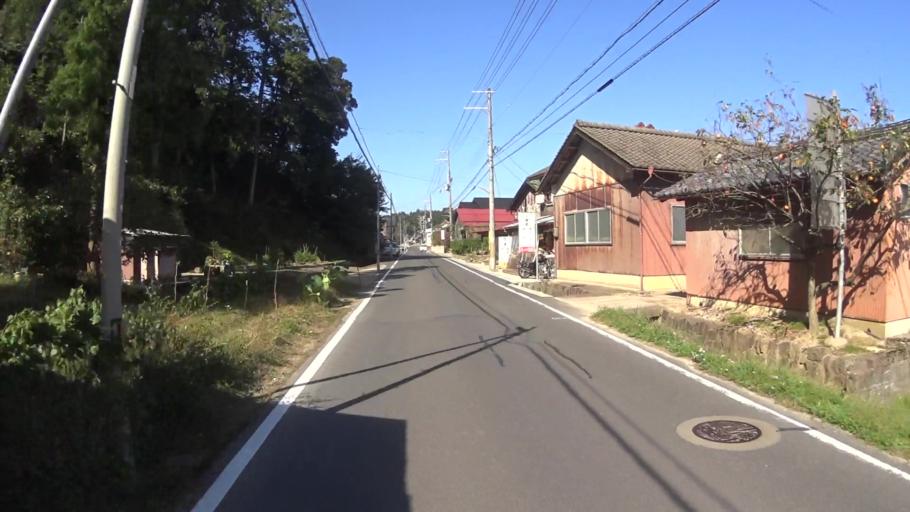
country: JP
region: Kyoto
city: Miyazu
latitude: 35.6754
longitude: 135.0802
